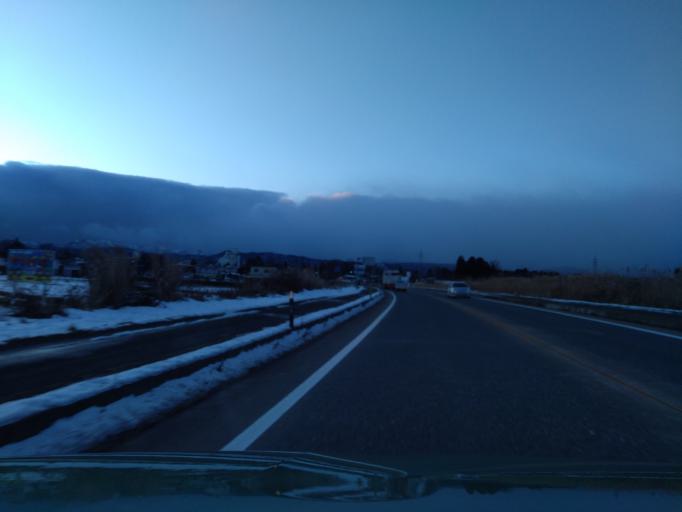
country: JP
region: Iwate
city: Shizukuishi
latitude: 39.7023
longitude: 140.9728
